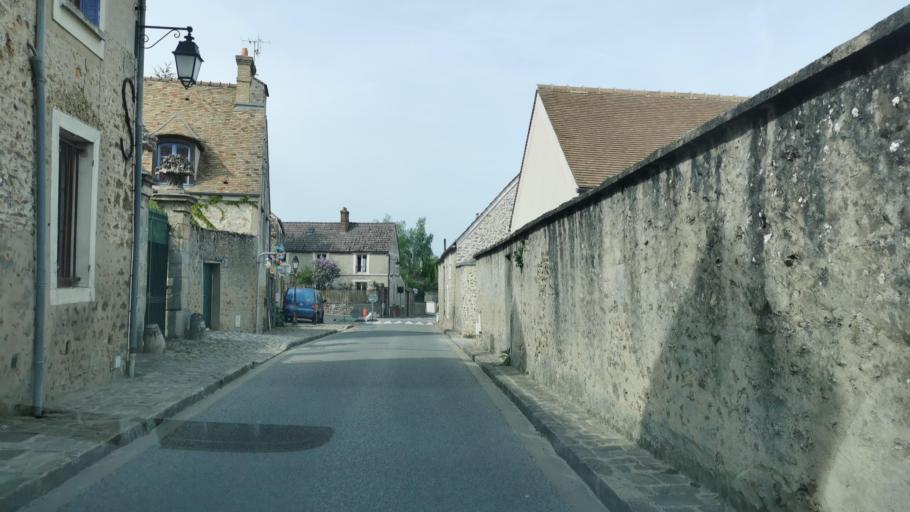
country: FR
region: Ile-de-France
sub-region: Departement des Yvelines
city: Jouars-Pontchartrain
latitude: 48.7795
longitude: 1.8742
